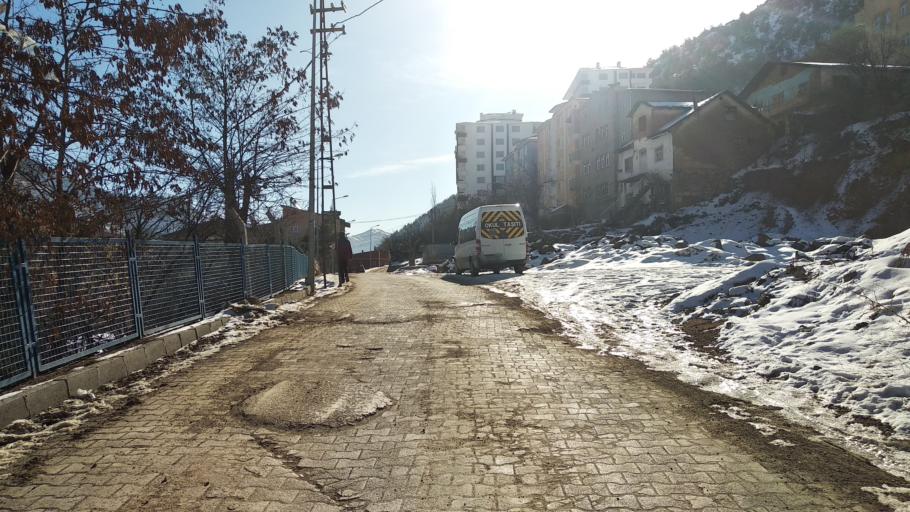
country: TR
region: Gumushane
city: Gumushkhane
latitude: 40.4558
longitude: 39.4873
